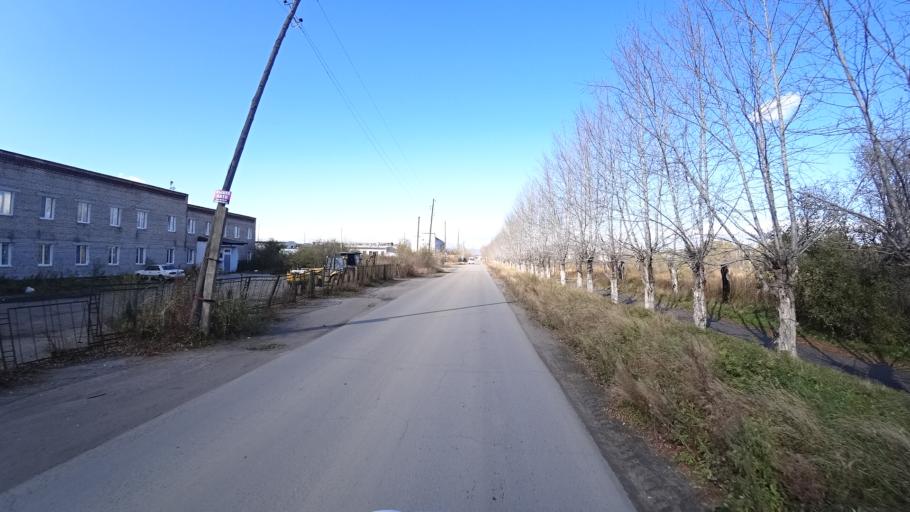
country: RU
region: Khabarovsk Krai
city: Amursk
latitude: 50.0960
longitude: 136.4971
